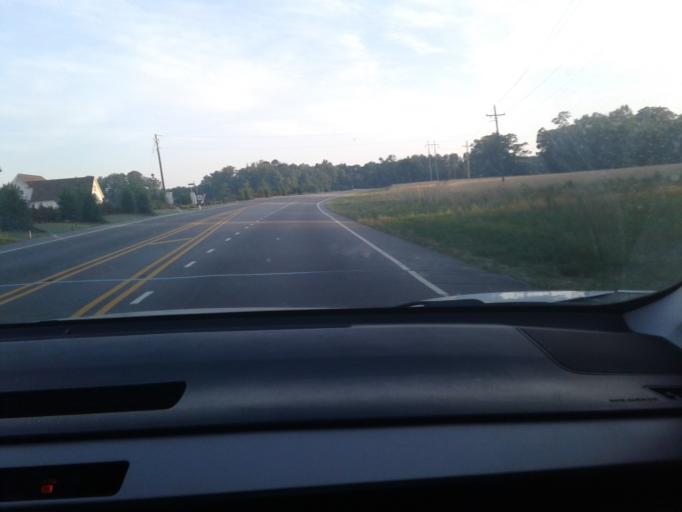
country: US
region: North Carolina
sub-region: Harnett County
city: Lillington
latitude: 35.4337
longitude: -78.8280
